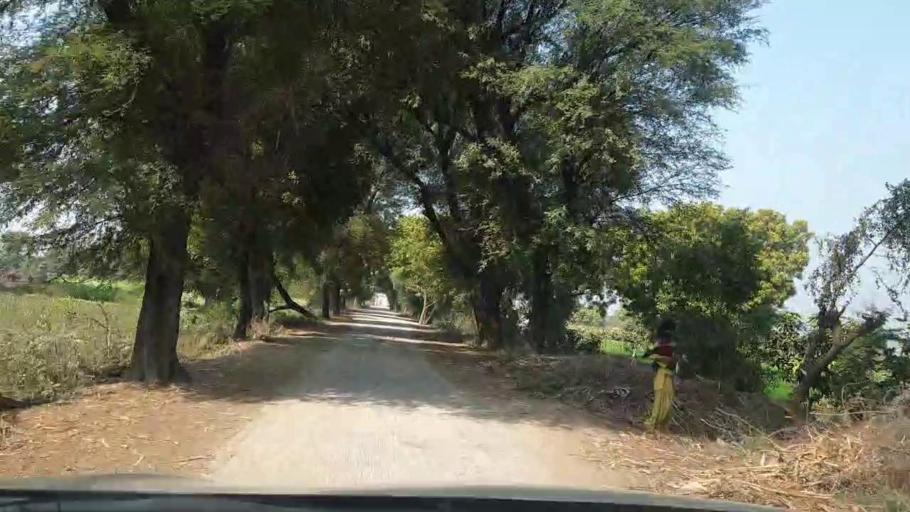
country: PK
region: Sindh
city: Tando Allahyar
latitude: 25.5312
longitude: 68.7711
